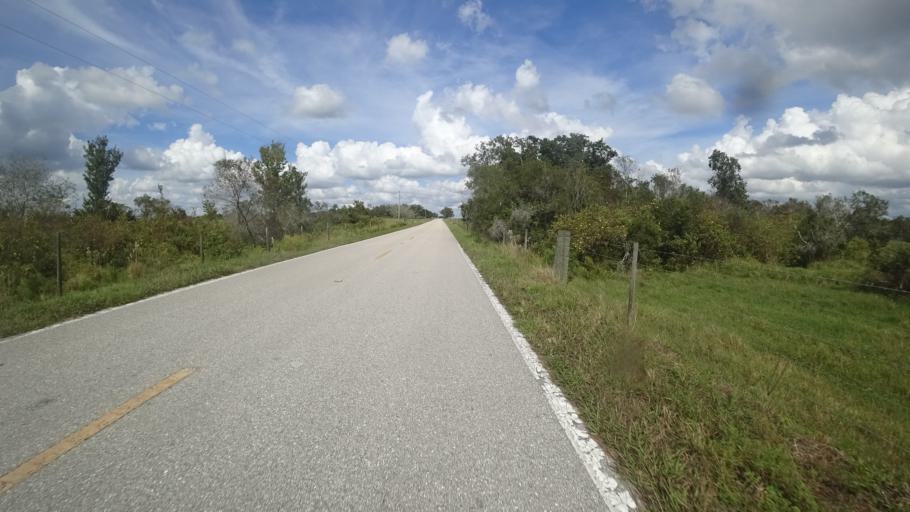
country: US
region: Florida
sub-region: Hillsborough County
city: Wimauma
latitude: 27.6224
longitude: -82.2309
